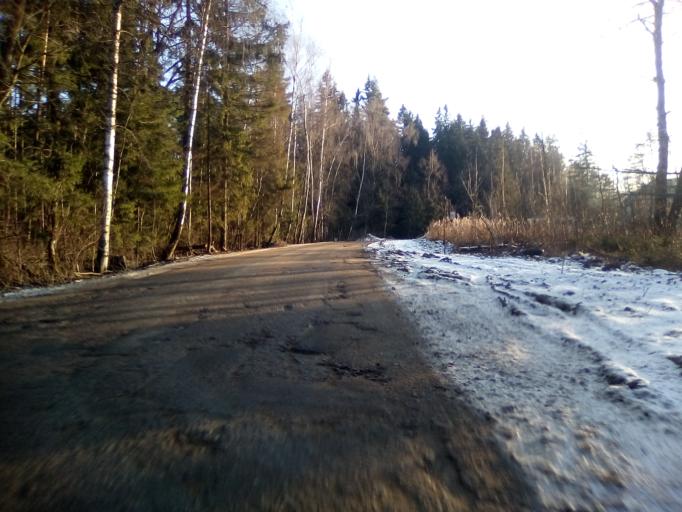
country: RU
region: Moskovskaya
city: Kokoshkino
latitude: 55.6308
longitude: 37.1506
